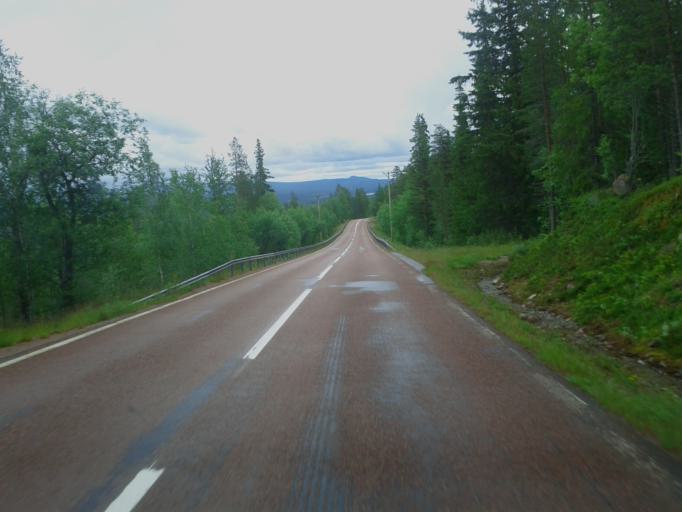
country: NO
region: Hedmark
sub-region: Trysil
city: Innbygda
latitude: 61.8527
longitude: 12.6247
